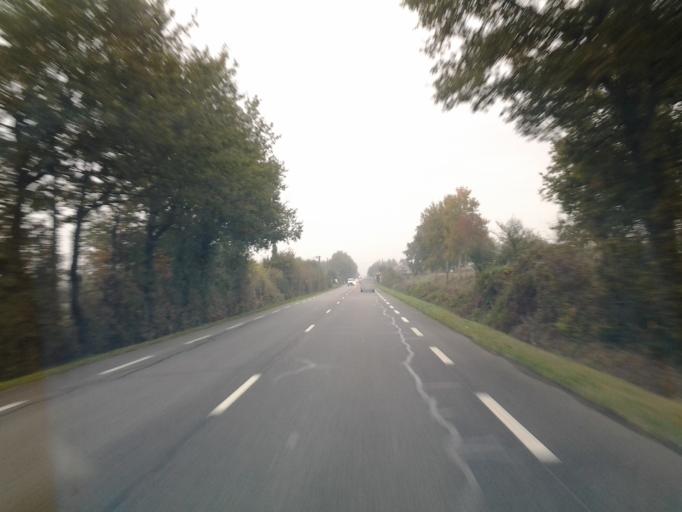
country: FR
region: Pays de la Loire
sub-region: Departement de la Vendee
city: Saint-Florent-des-Bois
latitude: 46.6084
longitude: -1.3423
